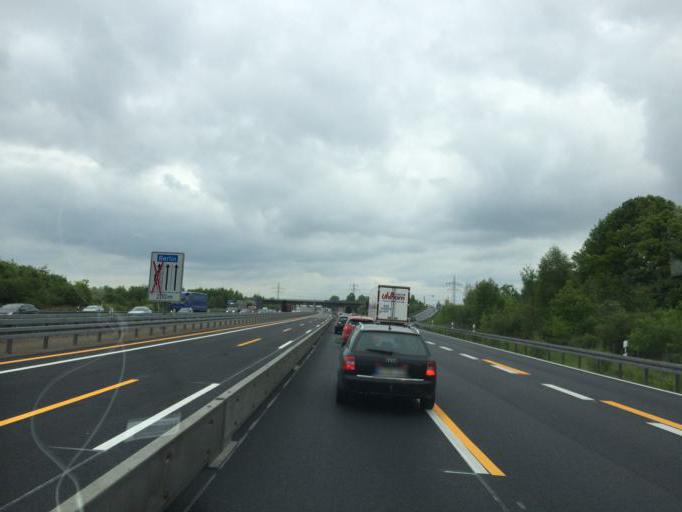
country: DE
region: Lower Saxony
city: Lehrte
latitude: 52.3905
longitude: 9.9567
